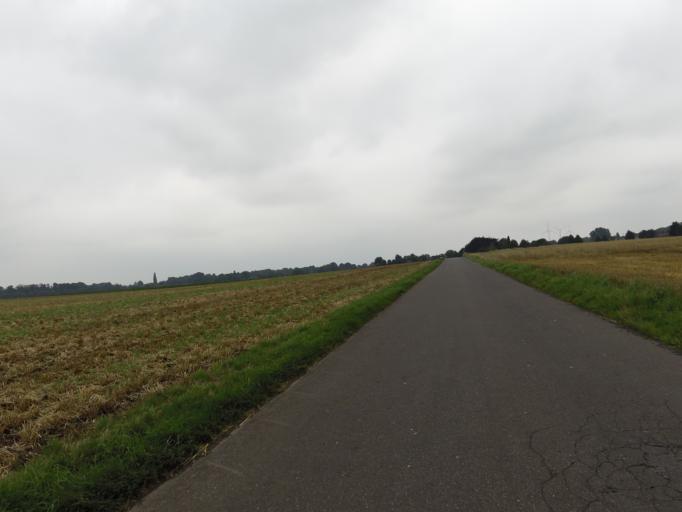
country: DE
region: North Rhine-Westphalia
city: Geilenkirchen
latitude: 50.9986
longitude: 6.1769
